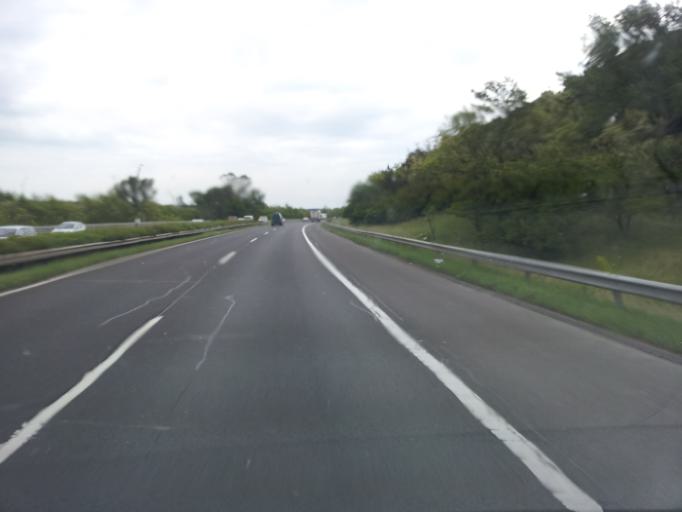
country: HU
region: Pest
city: Domony
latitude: 47.6231
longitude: 19.4144
